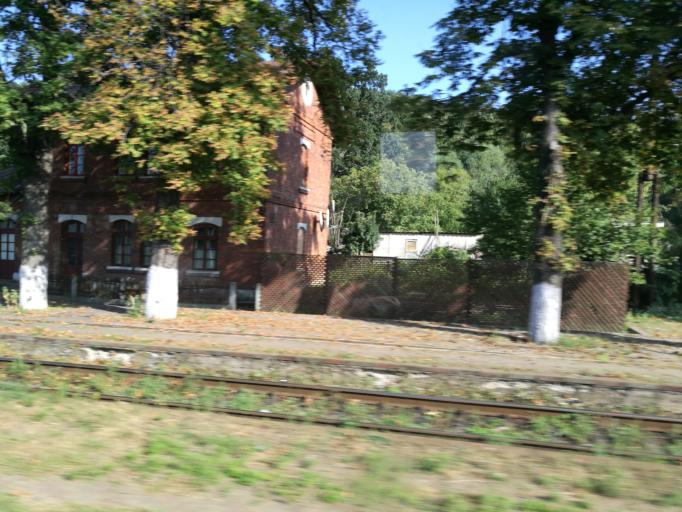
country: RO
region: Iasi
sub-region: Comuna Ciurea
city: Ciurea
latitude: 47.0129
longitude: 27.5694
